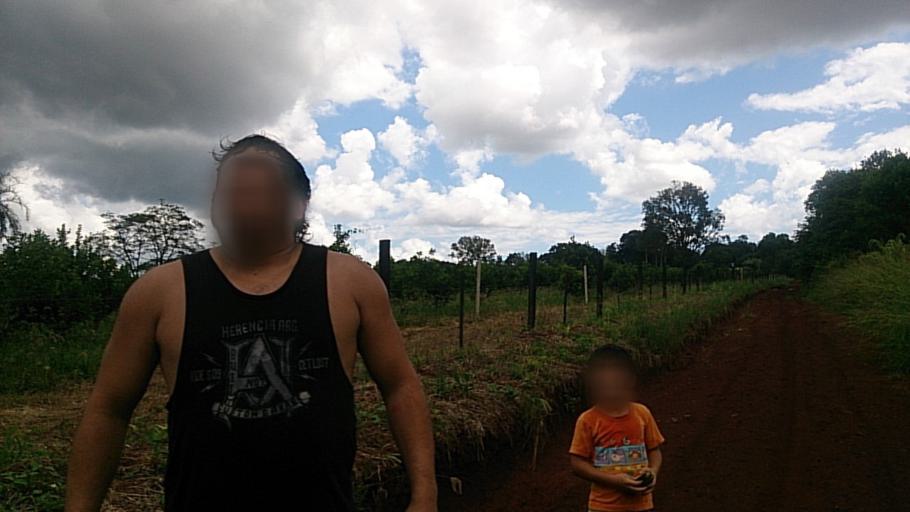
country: AR
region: Misiones
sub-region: Departamento de Obera
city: Obera
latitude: -27.5119
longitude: -55.1092
